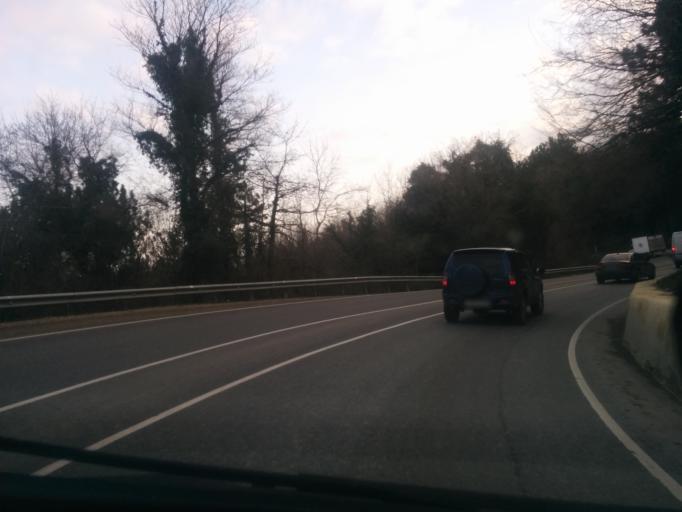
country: RU
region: Krasnodarskiy
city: Agoy
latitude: 44.1236
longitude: 39.0491
